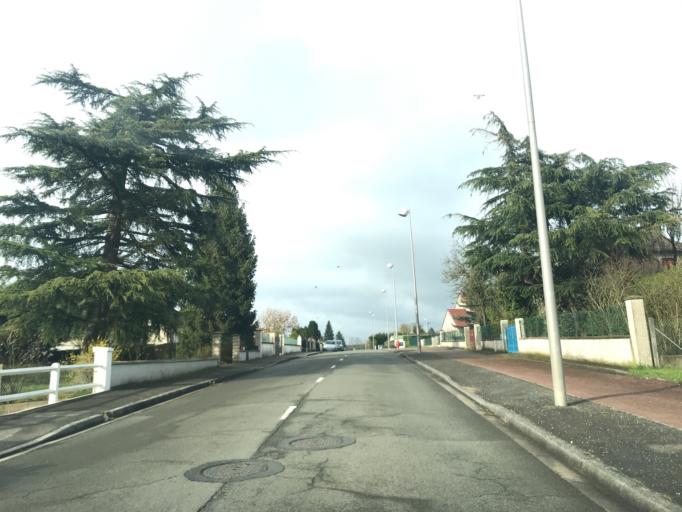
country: FR
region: Centre
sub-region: Departement du Loiret
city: Saint-Martin-sur-Ocre
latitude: 47.6812
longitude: 2.6548
